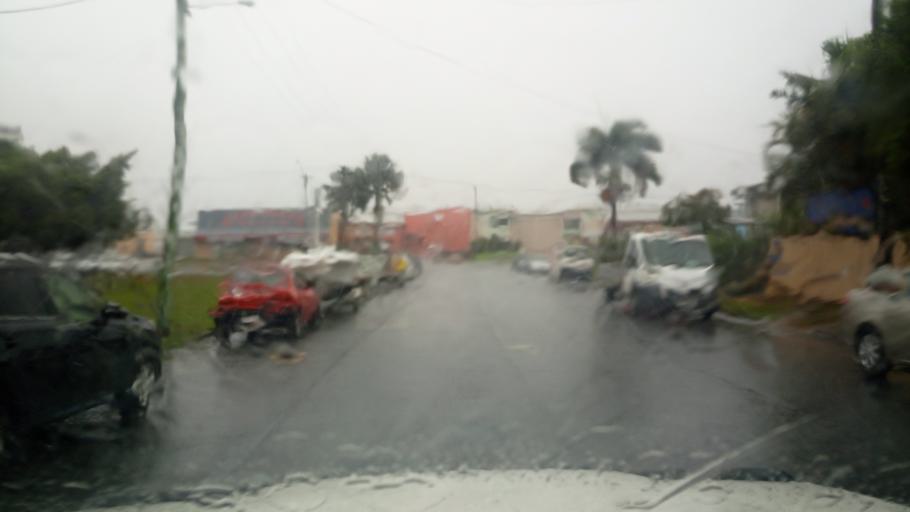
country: AU
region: Queensland
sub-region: Cairns
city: Woree
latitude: -16.9388
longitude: 145.7597
